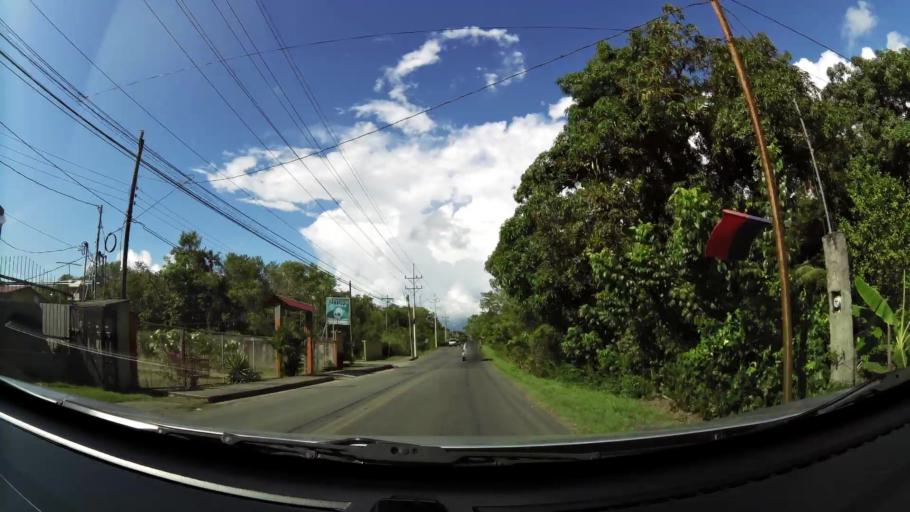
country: CR
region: Puntarenas
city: Quepos
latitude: 9.4467
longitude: -84.1661
